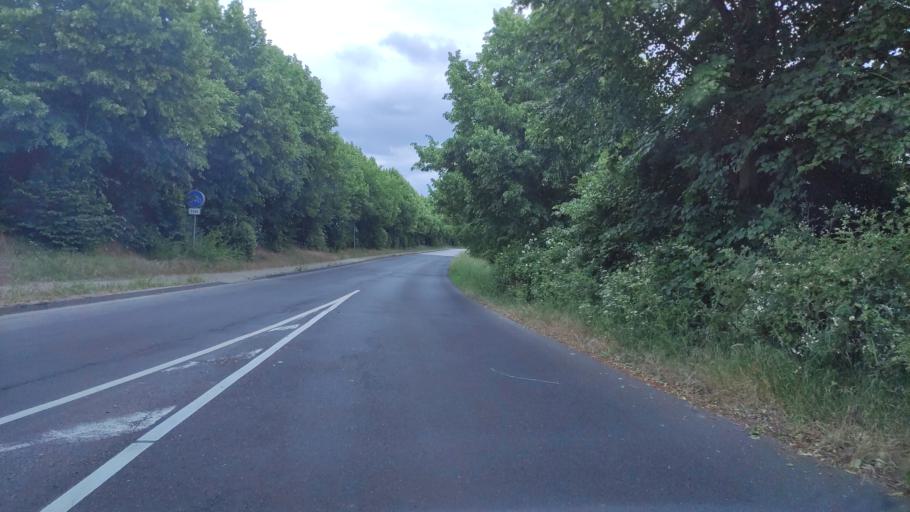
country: DE
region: North Rhine-Westphalia
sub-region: Regierungsbezirk Dusseldorf
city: Neubrueck
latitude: 51.1674
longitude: 6.6559
